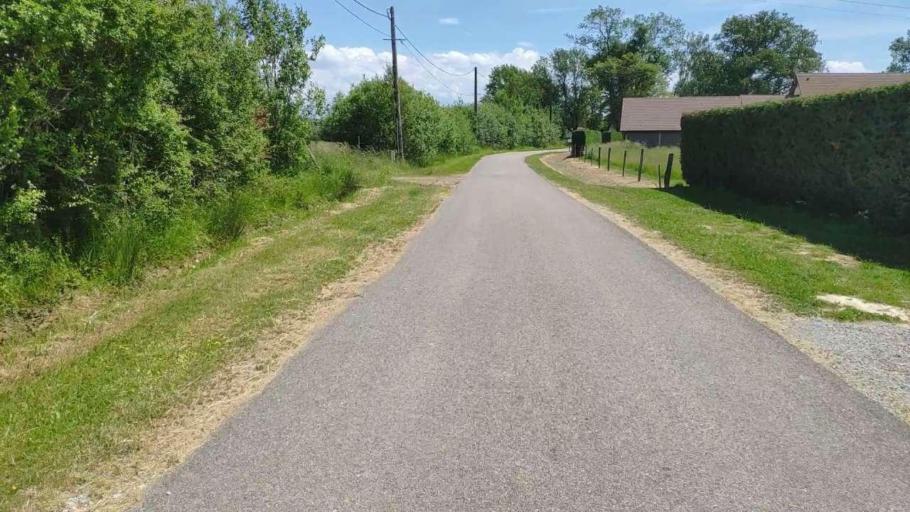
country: FR
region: Franche-Comte
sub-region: Departement du Jura
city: Bletterans
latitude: 46.7865
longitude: 5.4487
